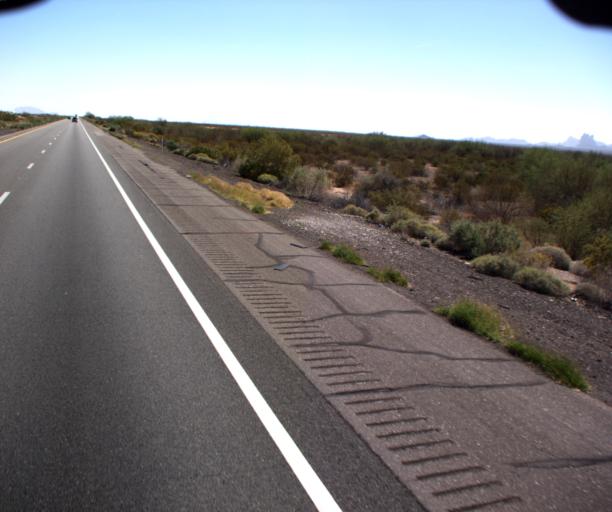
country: US
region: Arizona
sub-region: La Paz County
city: Salome
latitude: 33.5847
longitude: -113.4593
